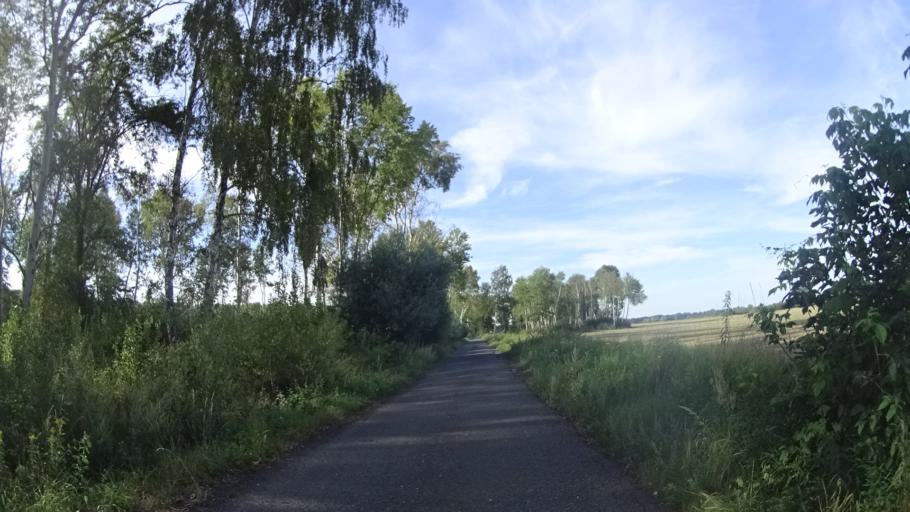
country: AT
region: Lower Austria
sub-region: Politischer Bezirk Ganserndorf
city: Drosing
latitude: 48.5782
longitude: 16.9530
